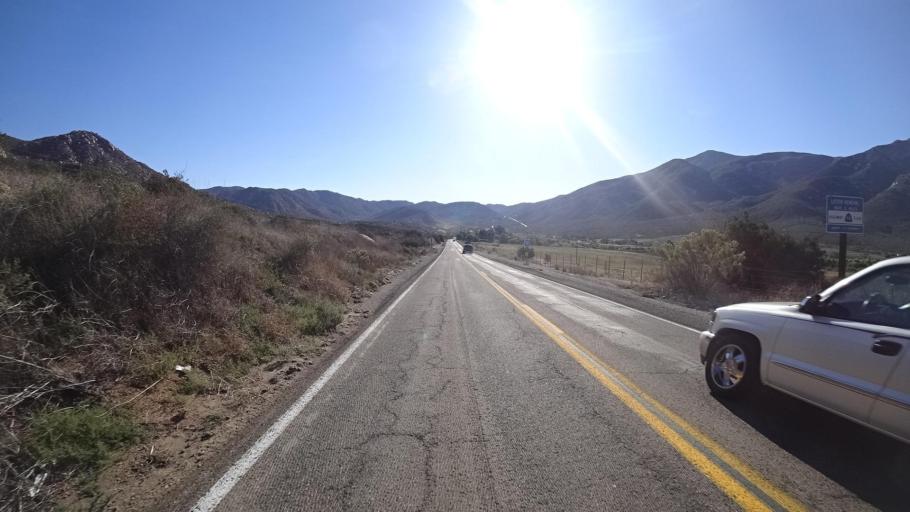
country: MX
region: Baja California
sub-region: Tecate
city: Lomas de Santa Anita
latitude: 32.6142
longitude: -116.7147
